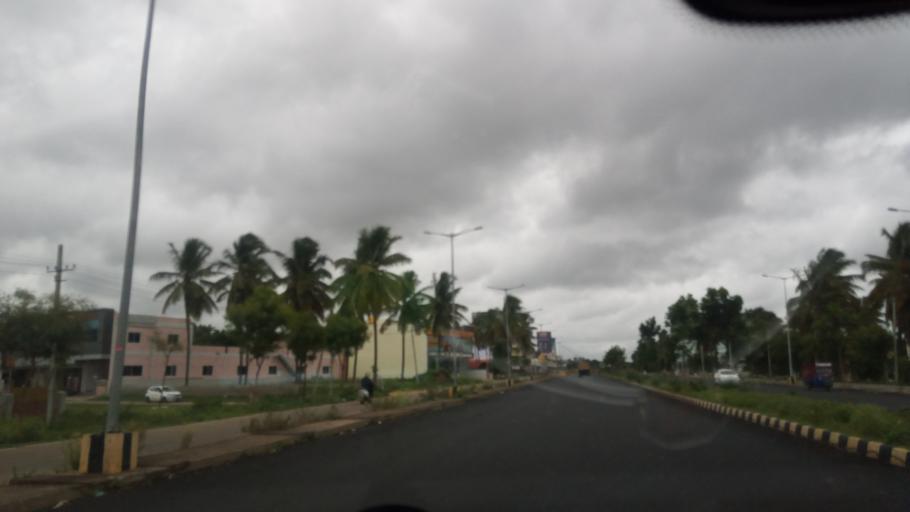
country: IN
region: Karnataka
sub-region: Mysore
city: Mysore
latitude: 12.2930
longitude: 76.6047
